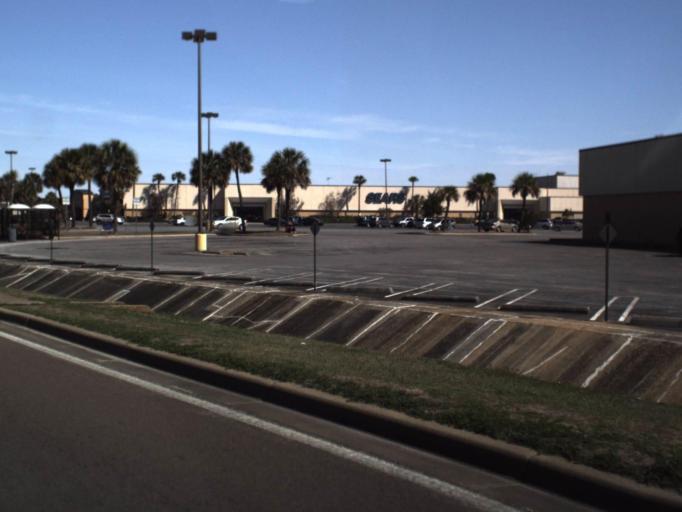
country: US
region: Florida
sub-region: Bay County
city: Panama City
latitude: 30.1841
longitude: -85.6500
